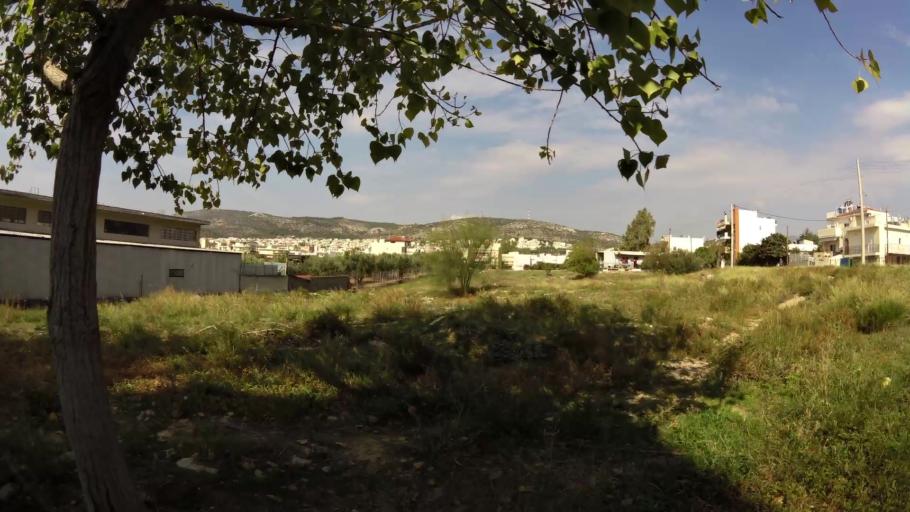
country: GR
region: Attica
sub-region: Nomarchia Athinas
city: Kamateron
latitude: 38.0493
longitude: 23.7101
